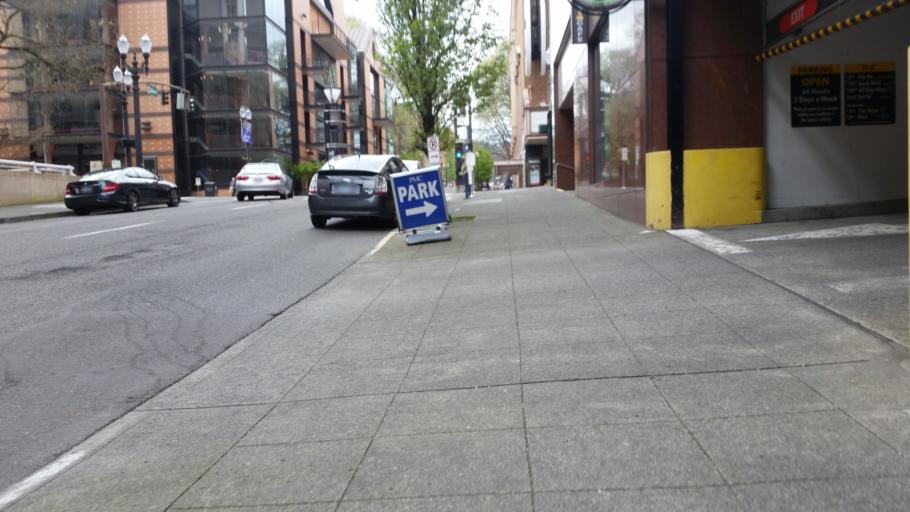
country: US
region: Oregon
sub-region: Multnomah County
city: Portland
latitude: 45.5166
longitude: -122.6807
